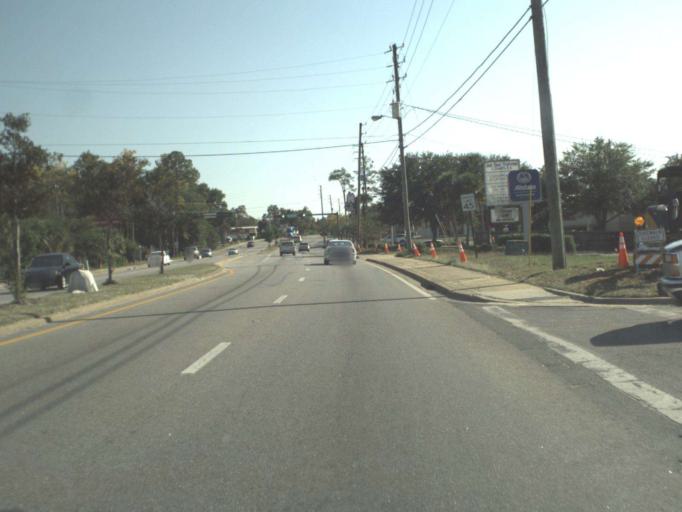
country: US
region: Florida
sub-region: Walton County
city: DeFuniak Springs
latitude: 30.7072
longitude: -86.1229
